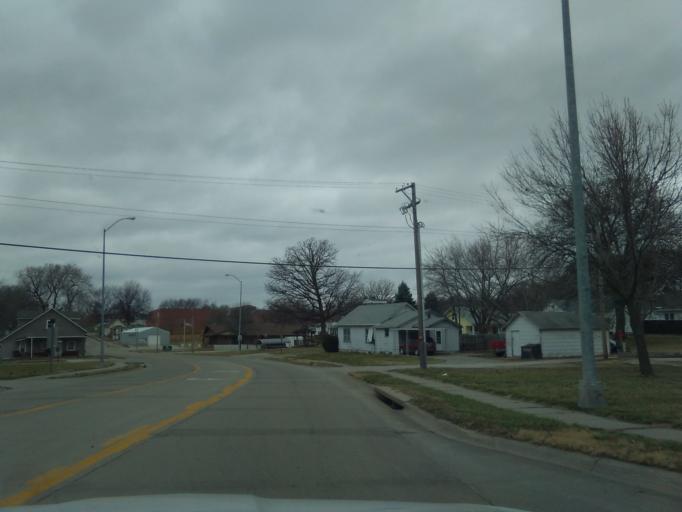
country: US
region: Nebraska
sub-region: Richardson County
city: Falls City
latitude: 40.0585
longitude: -95.5959
